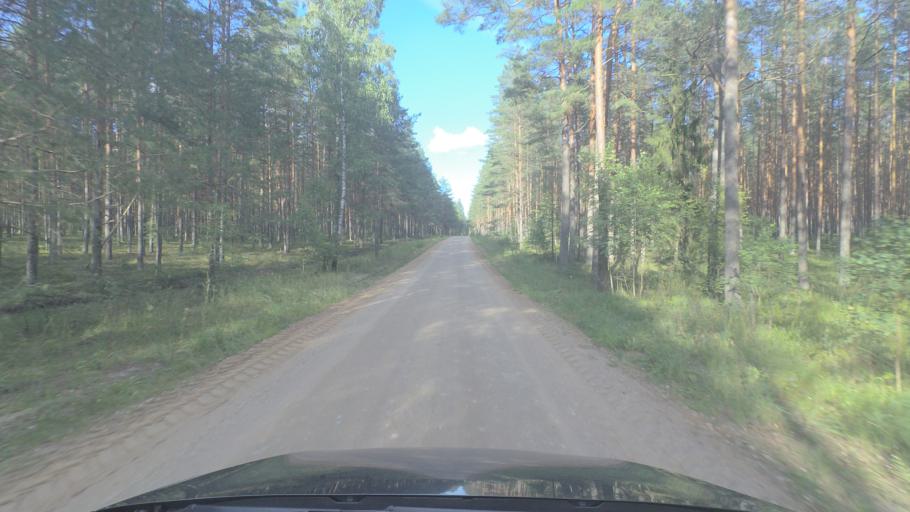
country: LT
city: Pabrade
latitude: 55.1594
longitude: 25.8091
